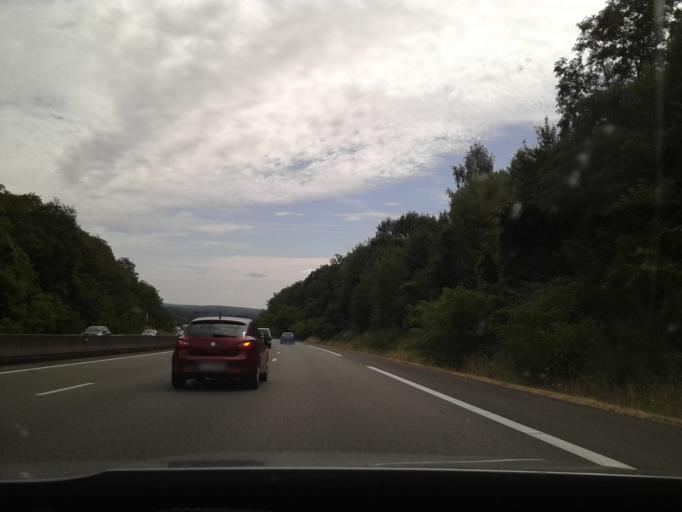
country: FR
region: Pays de la Loire
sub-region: Departement de la Sarthe
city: Sarge-les-le-Mans
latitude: 48.0492
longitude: 0.2757
